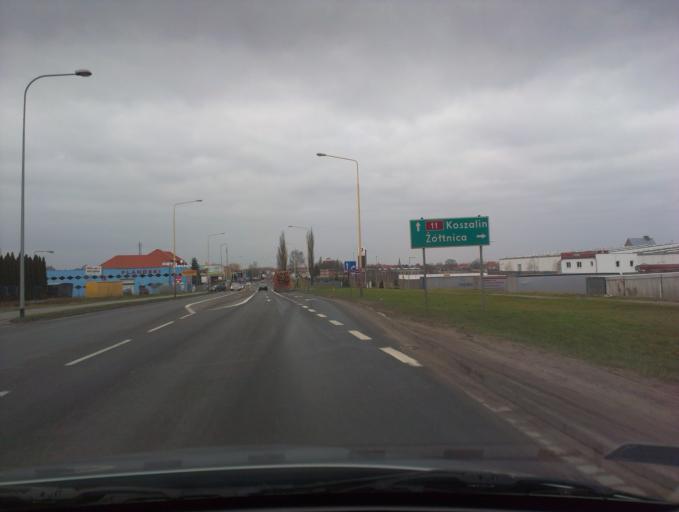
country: PL
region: West Pomeranian Voivodeship
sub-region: Powiat szczecinecki
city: Szczecinek
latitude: 53.6861
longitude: 16.7062
